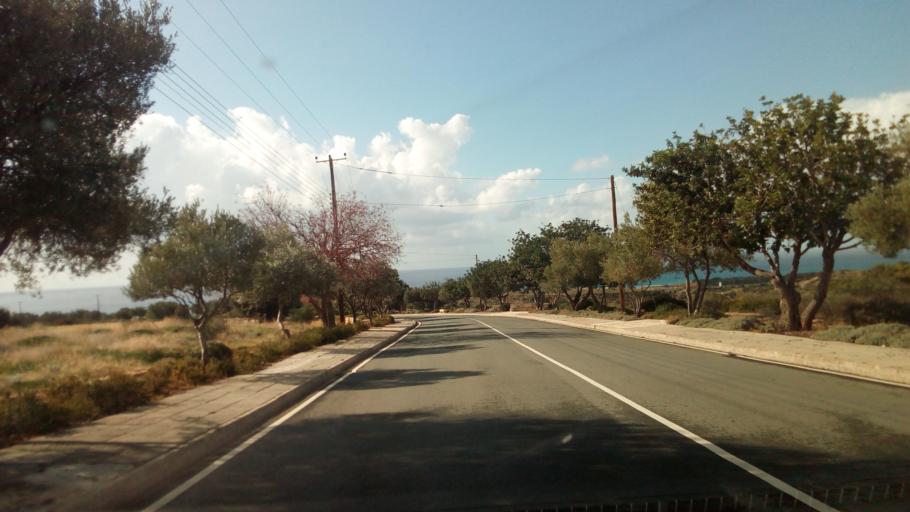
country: CY
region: Limassol
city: Pissouri
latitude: 34.6928
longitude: 32.5891
